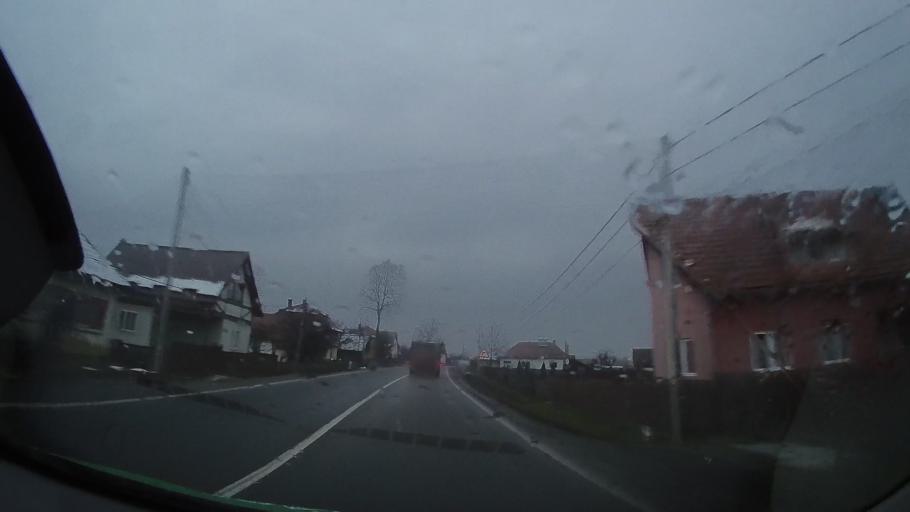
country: RO
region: Harghita
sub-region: Comuna Lazarea
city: Lazarea
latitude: 46.7567
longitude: 25.5180
